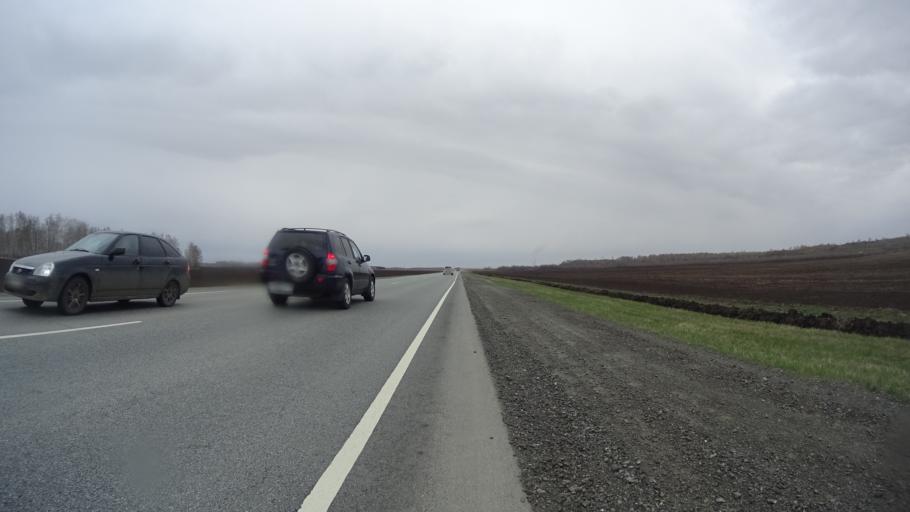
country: RU
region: Chelyabinsk
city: Krasnogorskiy
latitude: 54.5757
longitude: 61.2913
